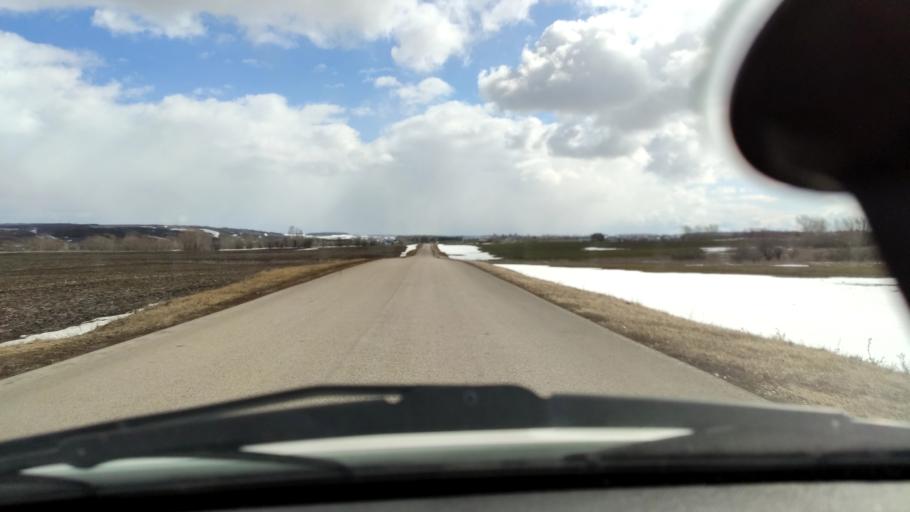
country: RU
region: Bashkortostan
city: Tolbazy
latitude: 54.1703
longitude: 55.9345
